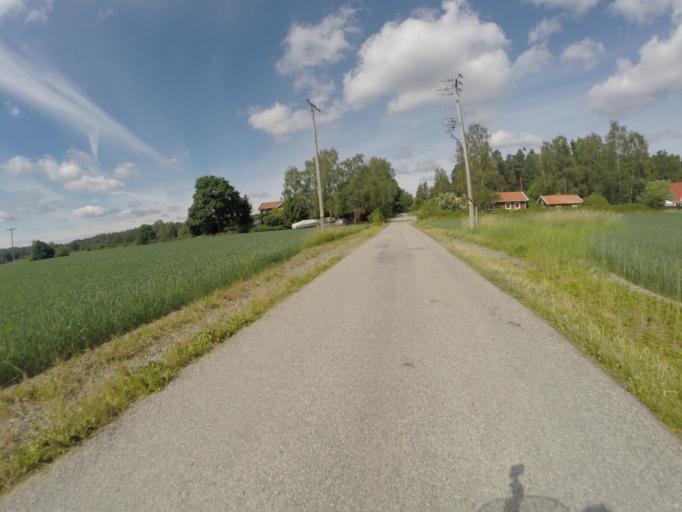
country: SE
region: Soedermanland
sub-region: Eskilstuna Kommun
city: Kvicksund
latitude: 59.4453
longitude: 16.3063
